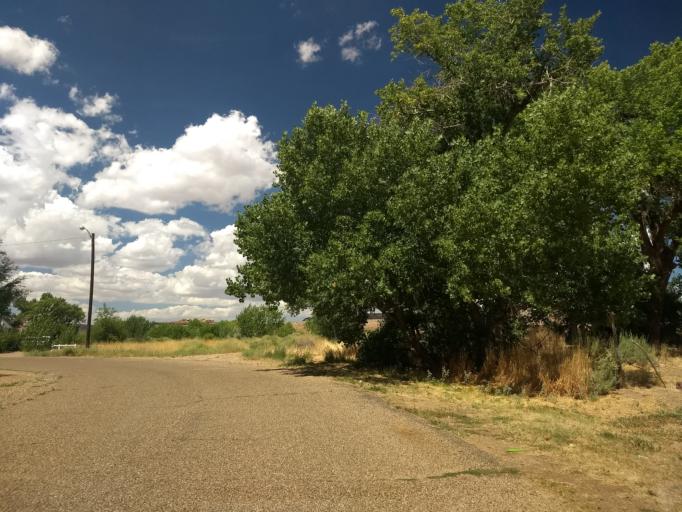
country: US
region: Arizona
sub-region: Coconino County
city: Fredonia
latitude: 36.9491
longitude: -112.5303
